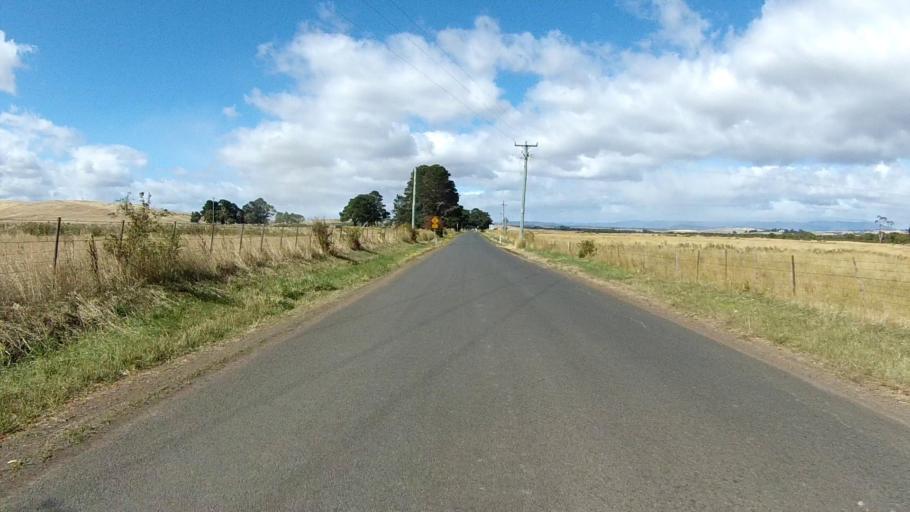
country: AU
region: Tasmania
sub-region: Northern Midlands
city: Evandale
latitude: -41.7490
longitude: 147.4887
